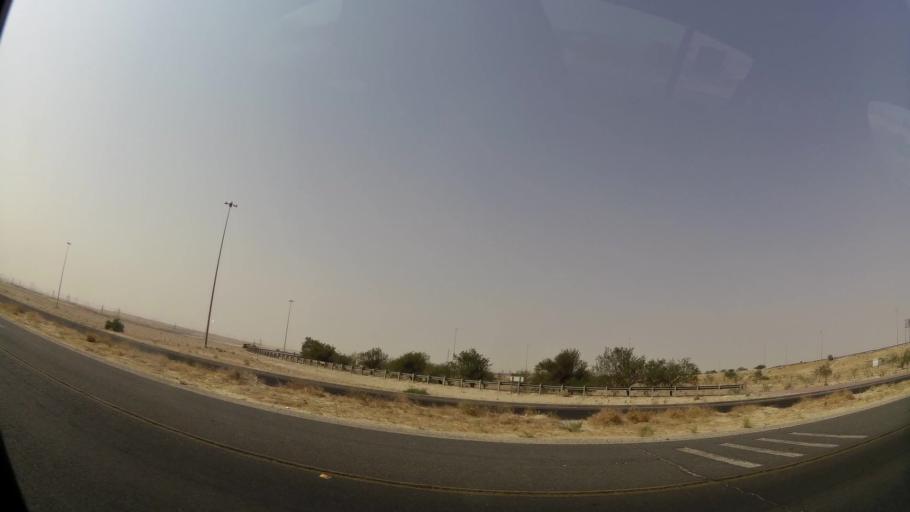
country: KW
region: Muhafazat al Jahra'
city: Al Jahra'
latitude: 29.3369
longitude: 47.6306
